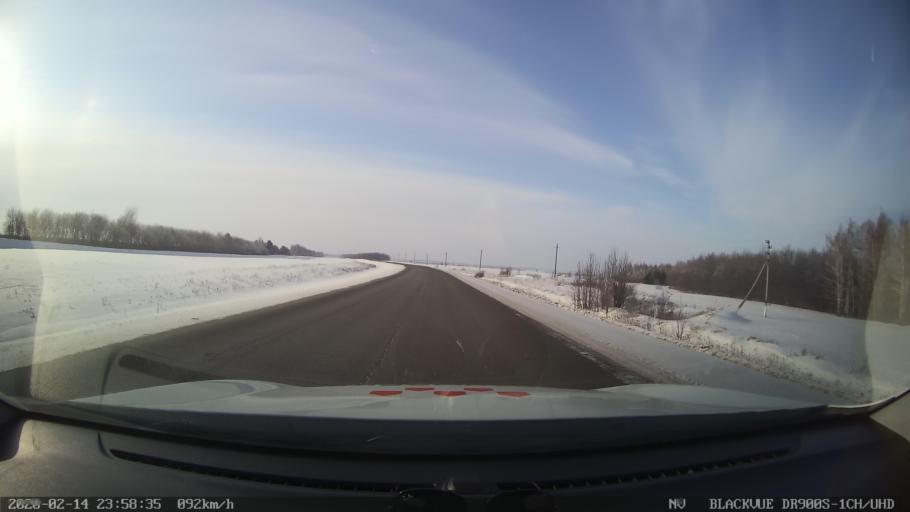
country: RU
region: Tatarstan
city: Kuybyshevskiy Zaton
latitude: 55.3415
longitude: 49.0840
